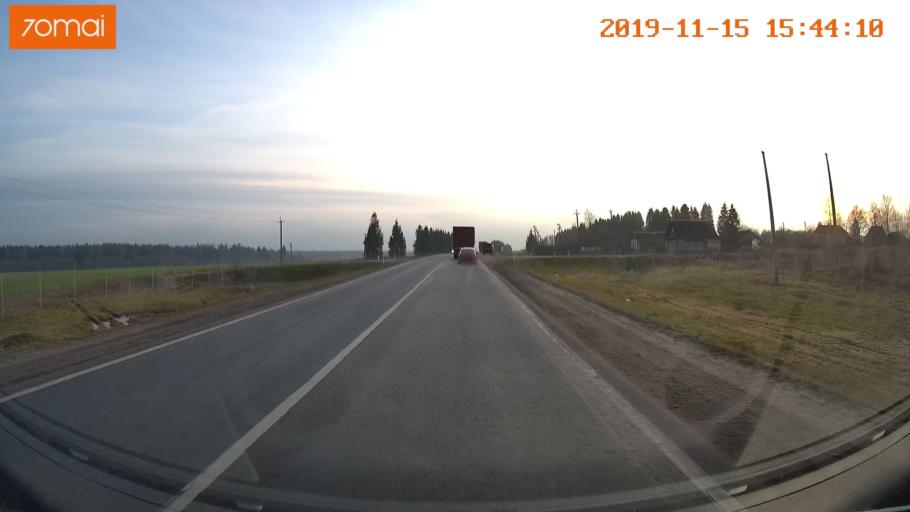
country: RU
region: Jaroslavl
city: Danilov
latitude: 57.9733
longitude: 40.0237
